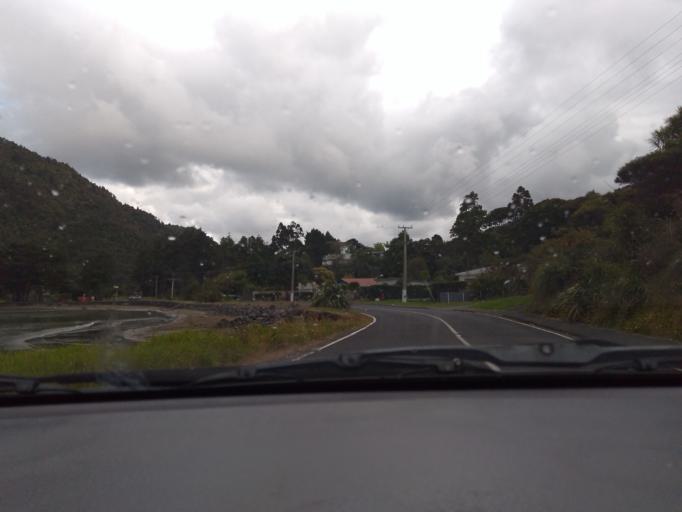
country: NZ
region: Auckland
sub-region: Auckland
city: Titirangi
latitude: -37.0007
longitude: 174.5723
